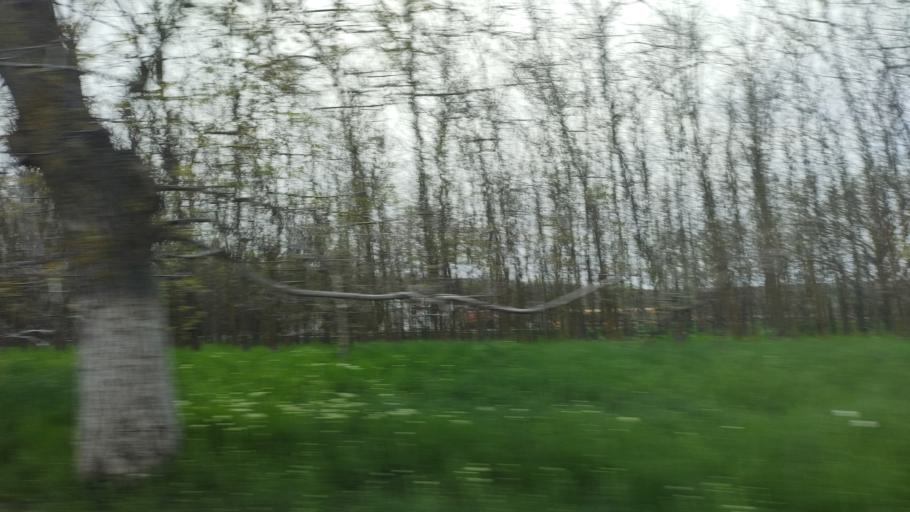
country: RO
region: Constanta
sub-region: Comuna Deleni
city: Pietreni
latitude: 44.0903
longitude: 28.0773
